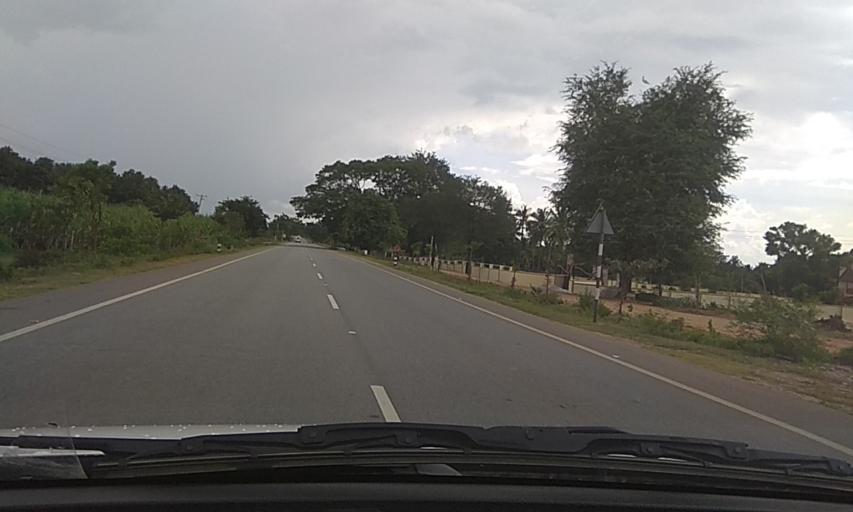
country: IN
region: Karnataka
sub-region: Tumkur
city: Kunigal
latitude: 12.8865
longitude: 77.0446
